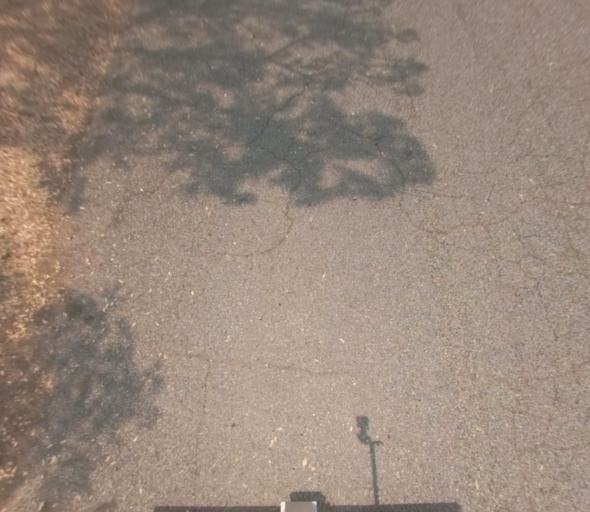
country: US
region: California
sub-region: Madera County
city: Coarsegold
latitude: 37.2371
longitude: -119.7126
